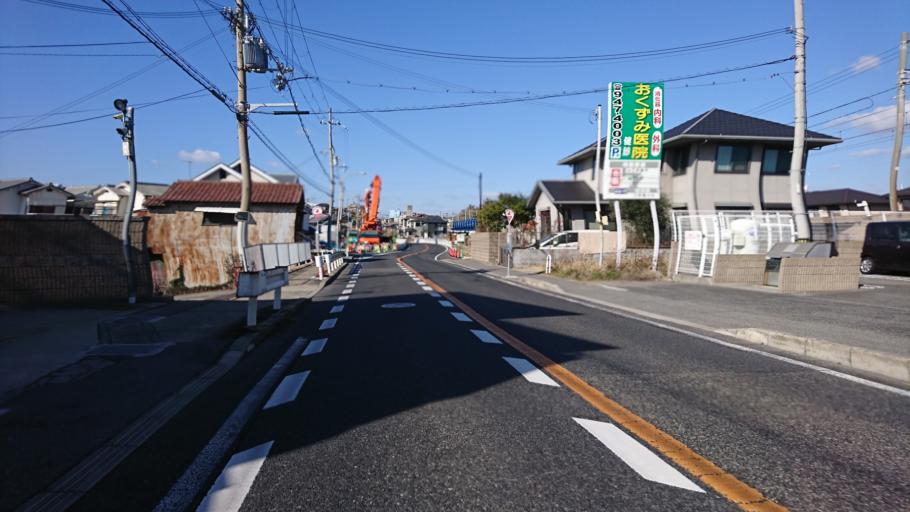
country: JP
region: Hyogo
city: Akashi
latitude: 34.6659
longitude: 134.9430
